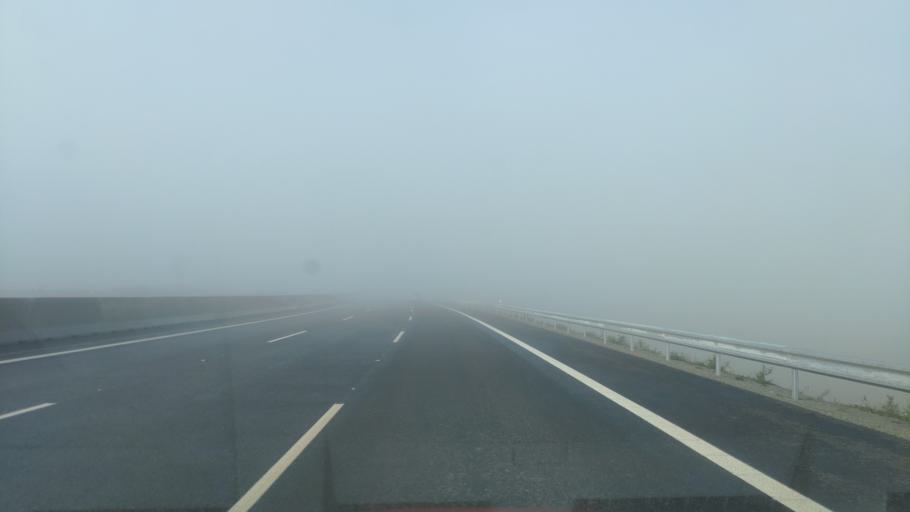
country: SK
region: Kosicky
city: Kosice
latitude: 48.7316
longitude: 21.4030
